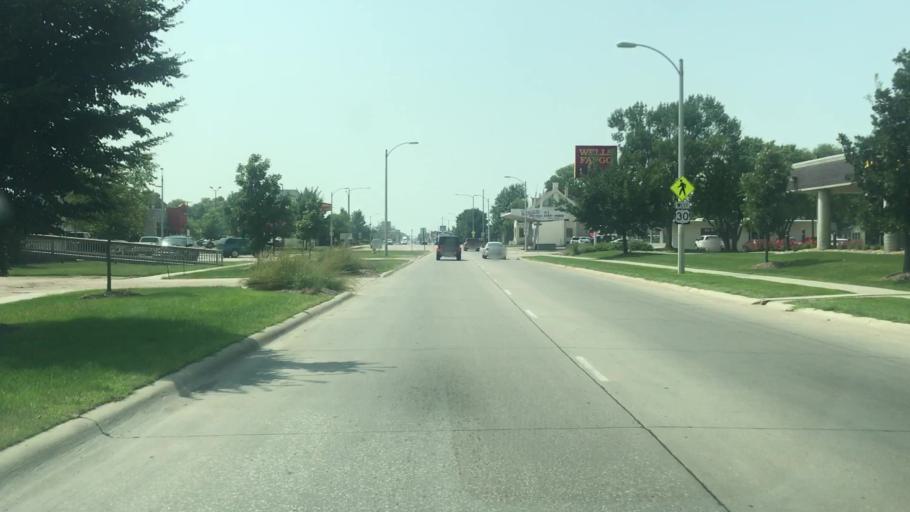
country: US
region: Nebraska
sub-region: Hall County
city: Grand Island
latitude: 40.9213
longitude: -98.3484
